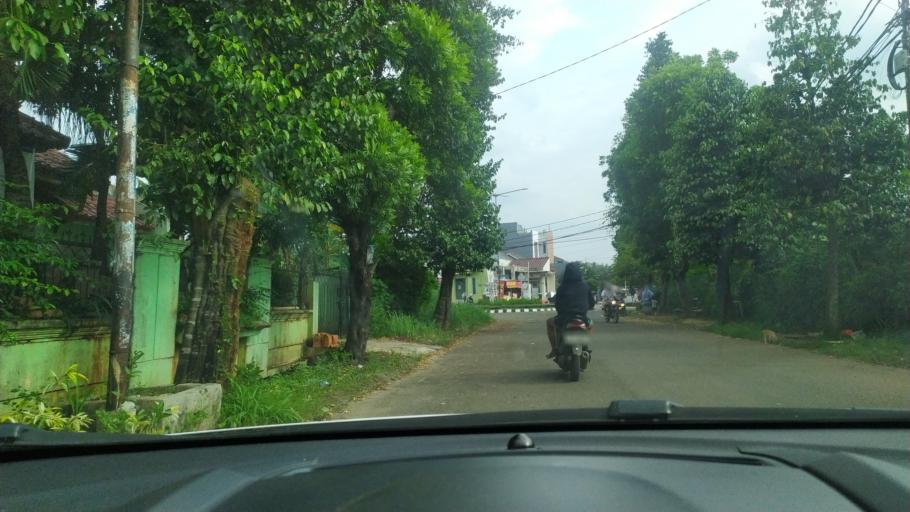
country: ID
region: West Java
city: Pamulang
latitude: -6.3565
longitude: 106.7456
